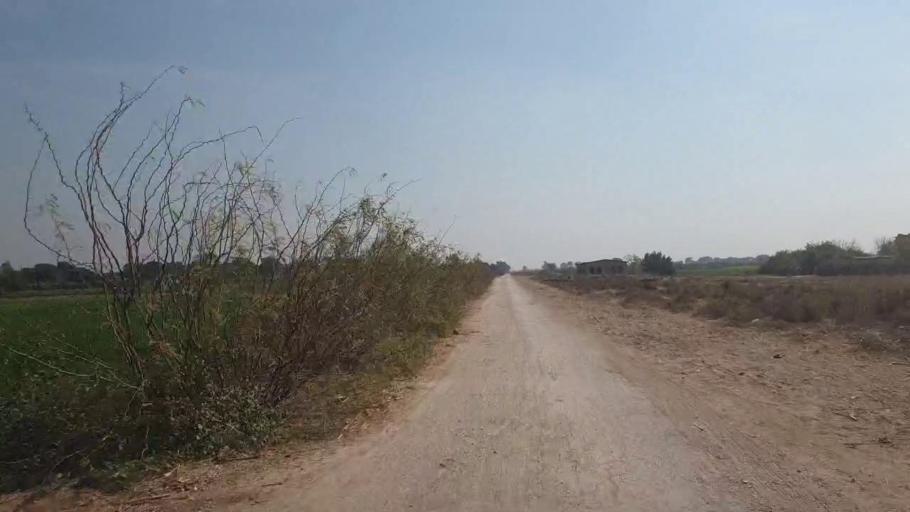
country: PK
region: Sindh
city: Chambar
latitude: 25.3611
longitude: 68.8001
